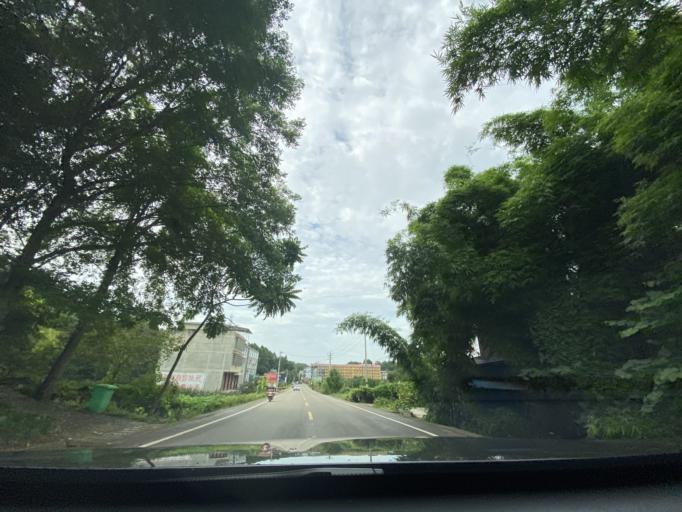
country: CN
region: Sichuan
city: Jiancheng
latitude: 30.4824
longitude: 104.6338
